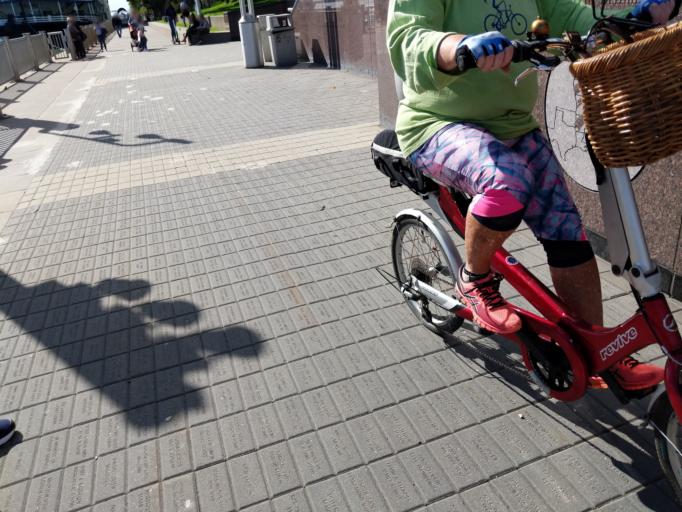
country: US
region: Michigan
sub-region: Wayne County
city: Detroit
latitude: 42.3264
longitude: -83.0440
